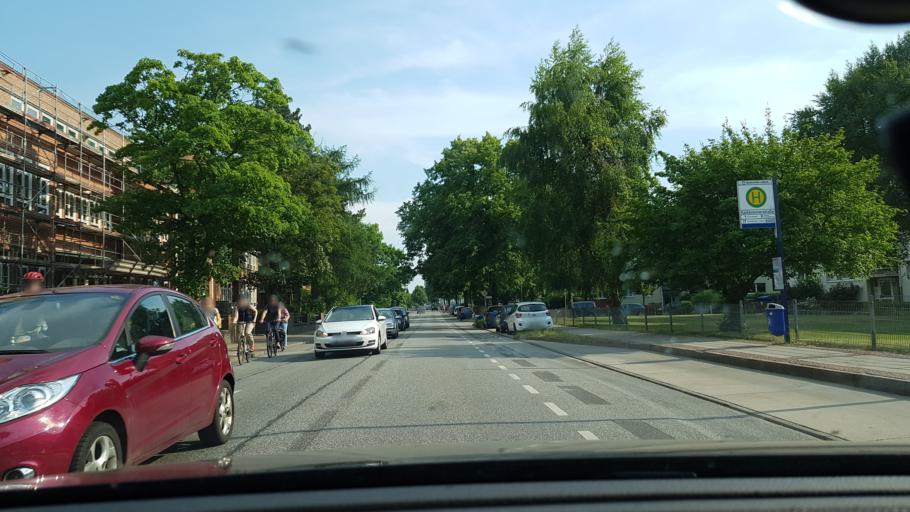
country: DE
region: Schleswig-Holstein
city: Luebeck
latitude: 53.8478
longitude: 10.6989
